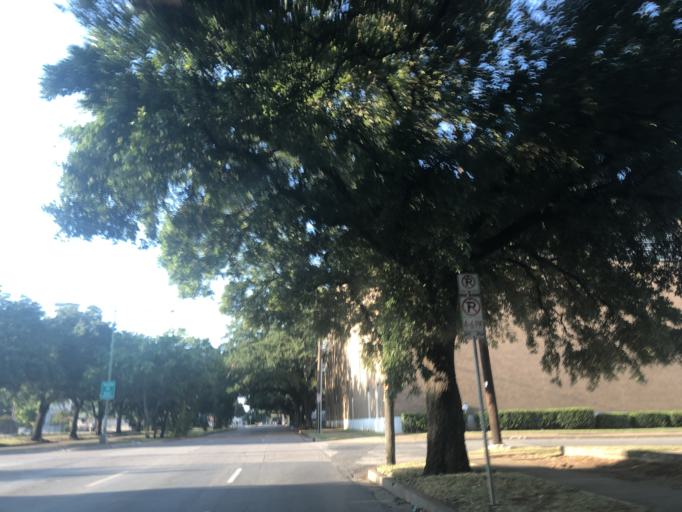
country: US
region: Texas
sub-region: Dallas County
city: Dallas
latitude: 32.7466
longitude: -96.8247
